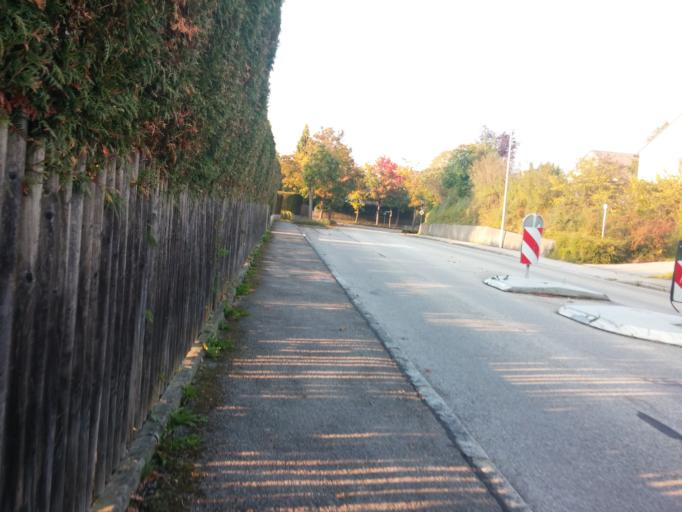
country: DE
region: Bavaria
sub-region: Upper Bavaria
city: Zorneding
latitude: 48.0943
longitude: 11.8305
